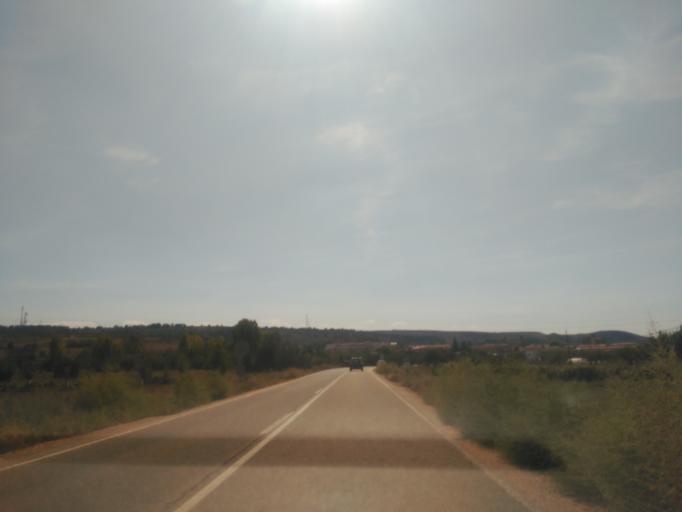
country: ES
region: Castille and Leon
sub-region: Provincia de Soria
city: El Burgo de Osma
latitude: 41.5954
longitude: -3.0595
